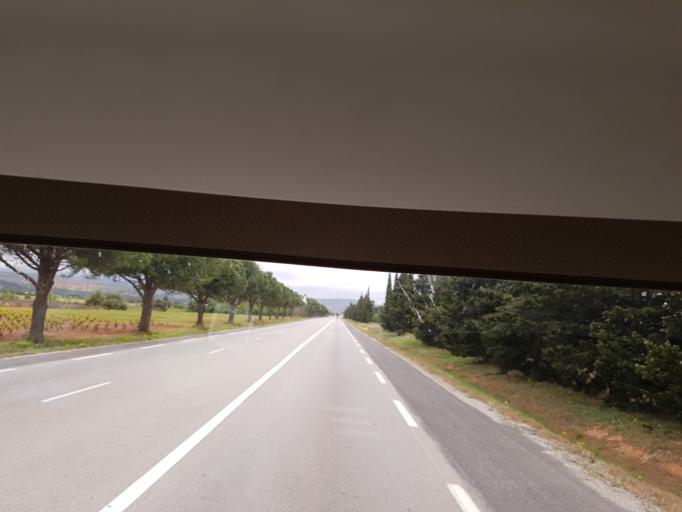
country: FR
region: Languedoc-Roussillon
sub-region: Departement des Pyrenees-Orientales
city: Salses-le-Chateau
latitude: 42.8148
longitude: 2.9144
